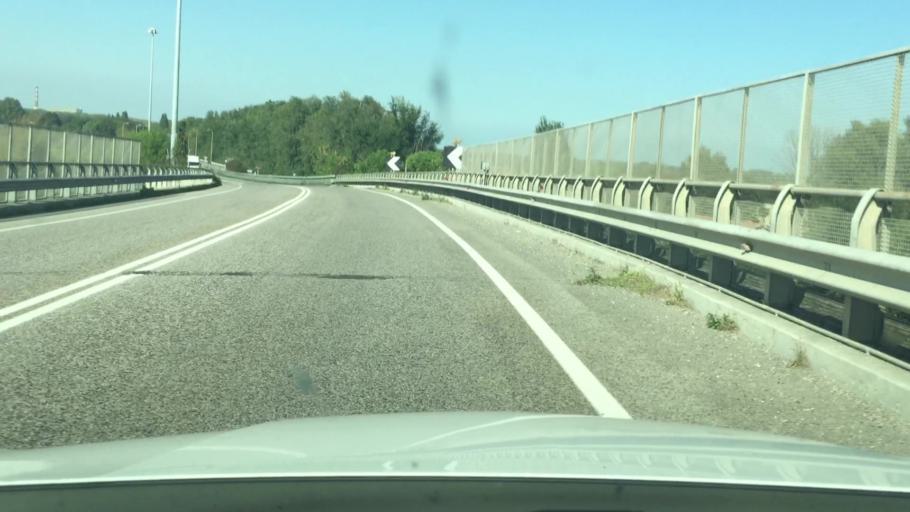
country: IT
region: Emilia-Romagna
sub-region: Provincia di Ravenna
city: Ravenna
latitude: 44.4582
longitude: 12.2088
